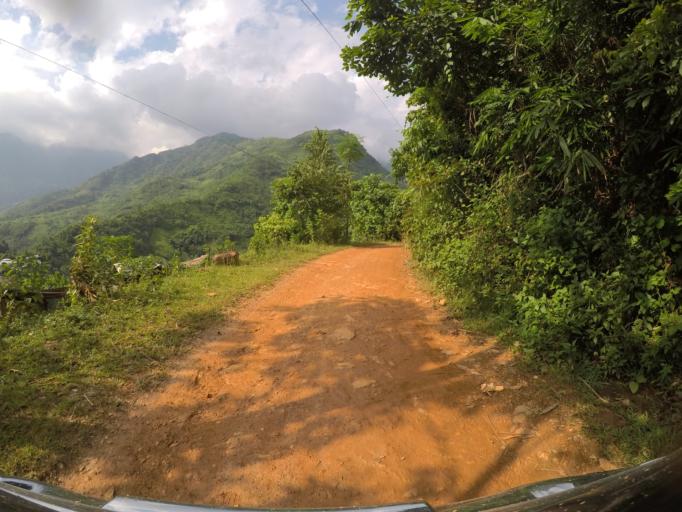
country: VN
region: Yen Bai
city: Son Thinh
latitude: 21.6800
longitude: 104.5933
